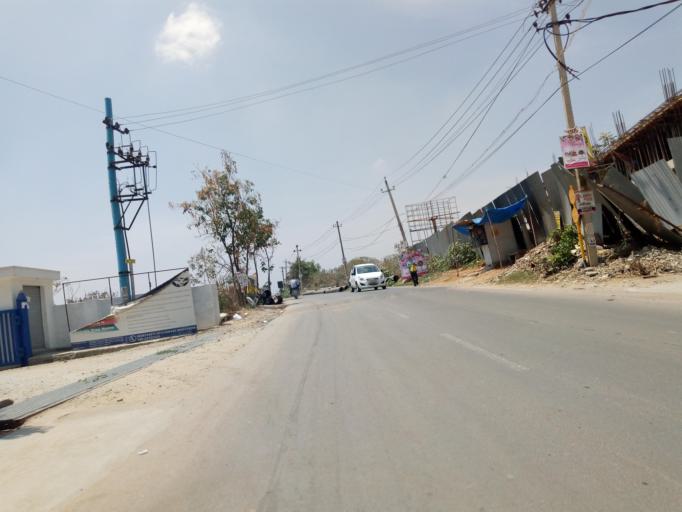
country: IN
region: Karnataka
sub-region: Bangalore Urban
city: Bangalore
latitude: 12.8854
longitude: 77.6559
